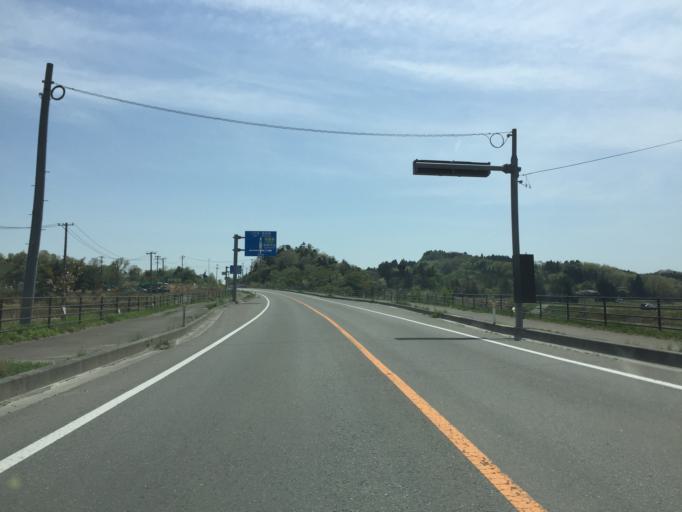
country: JP
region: Miyagi
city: Marumori
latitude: 37.8583
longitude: 140.9198
